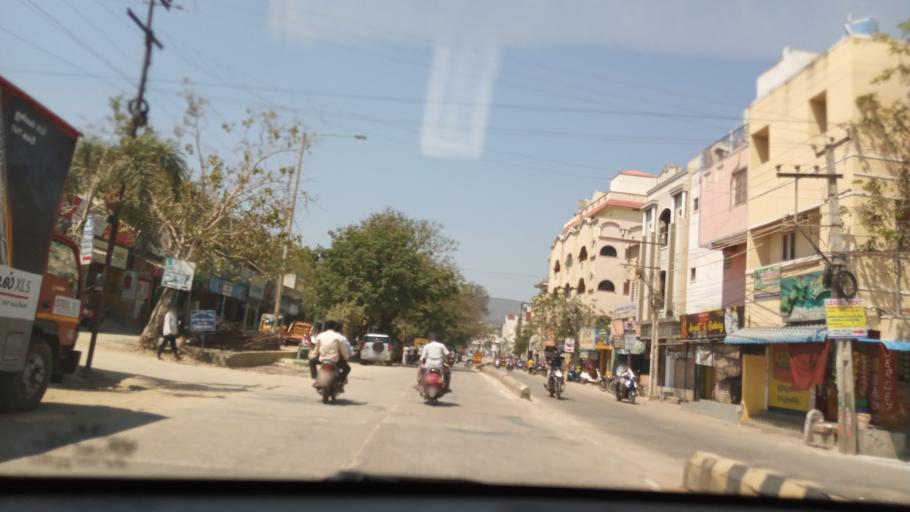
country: IN
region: Andhra Pradesh
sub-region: Chittoor
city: Tirupati
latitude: 13.6203
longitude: 79.4177
